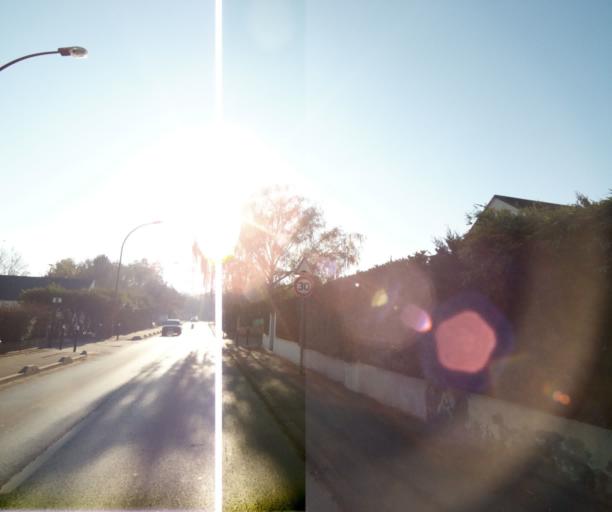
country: FR
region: Ile-de-France
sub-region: Departement du Val-d'Oise
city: Gonesse
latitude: 48.9936
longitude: 2.4319
